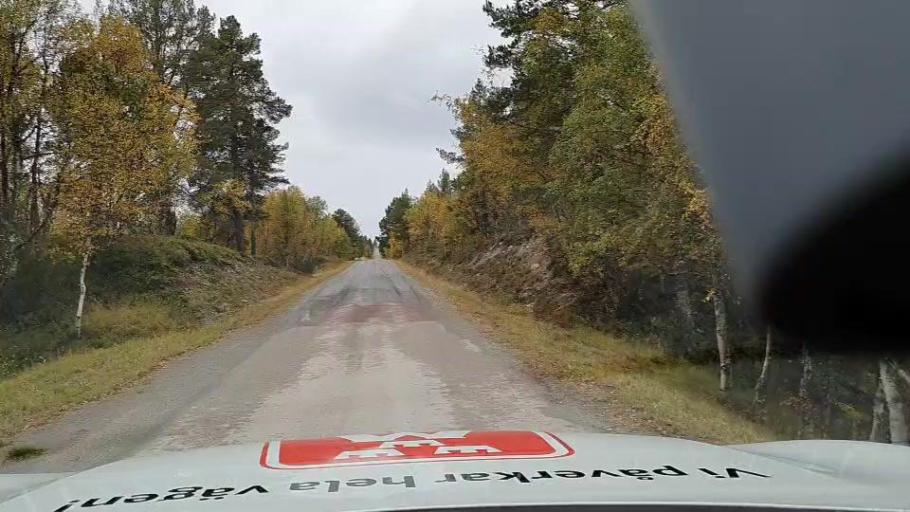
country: NO
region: Hedmark
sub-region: Engerdal
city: Engerdal
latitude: 62.1285
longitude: 12.8924
